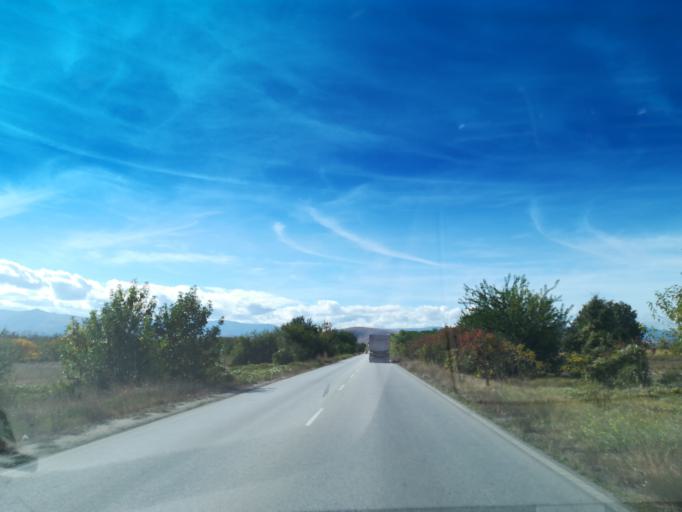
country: BG
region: Plovdiv
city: Stamboliyski
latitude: 42.1139
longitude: 24.5230
